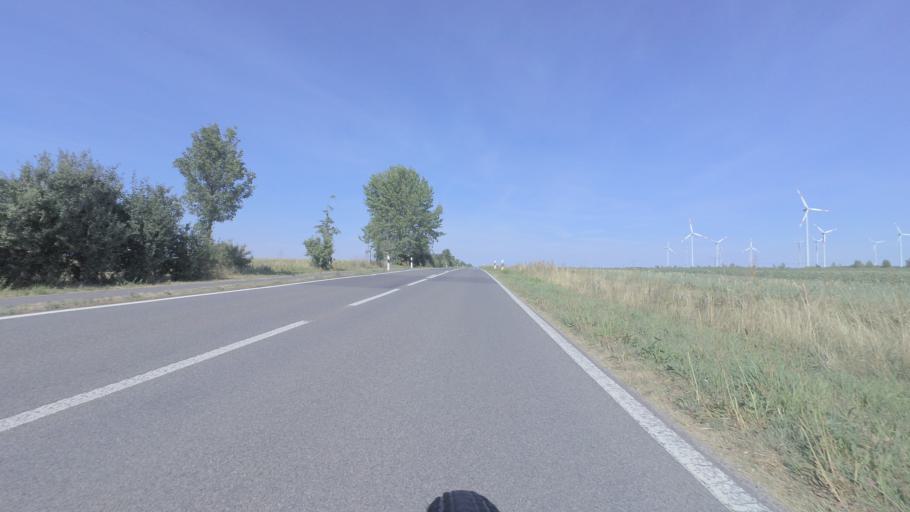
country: DE
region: Brandenburg
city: Trebbin
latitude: 52.1978
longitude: 13.2723
